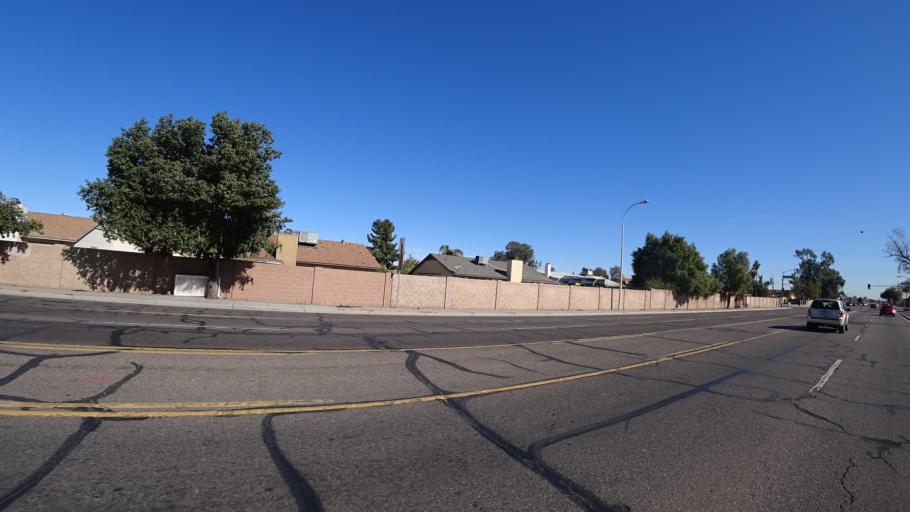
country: US
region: Arizona
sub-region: Maricopa County
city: Tolleson
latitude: 33.4944
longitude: -112.2309
